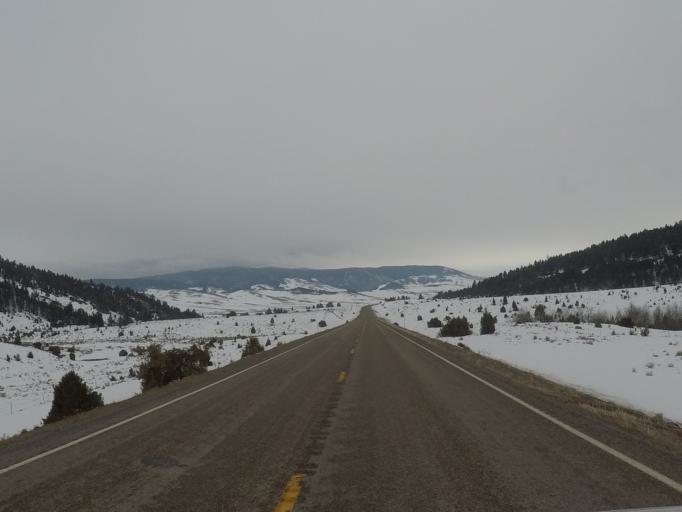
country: US
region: Montana
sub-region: Meagher County
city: White Sulphur Springs
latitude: 46.6146
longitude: -110.8442
